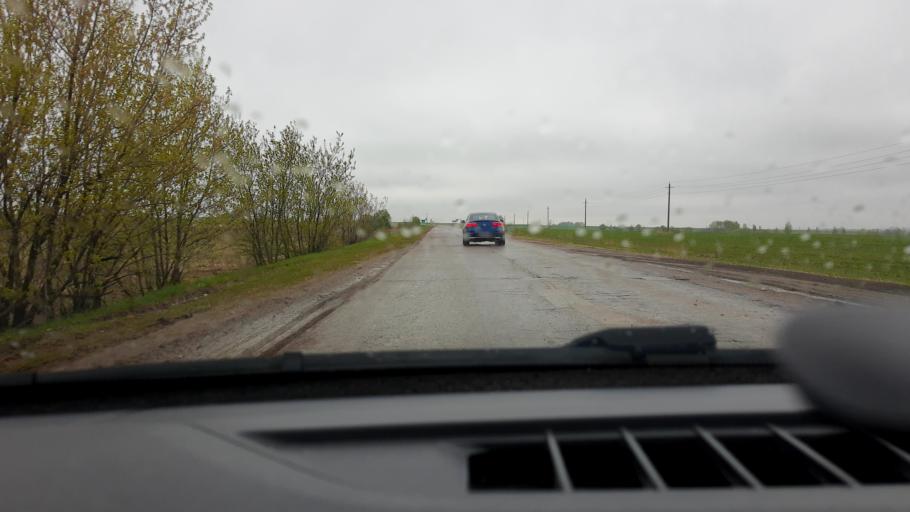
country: RU
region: Nizjnij Novgorod
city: Dal'neye Konstantinovo
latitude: 55.7593
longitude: 44.2316
